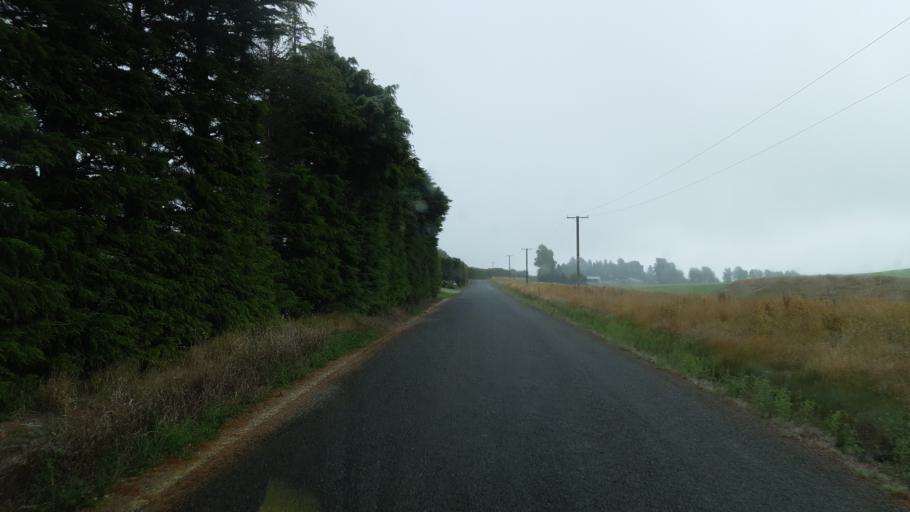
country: NZ
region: Otago
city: Oamaru
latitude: -44.9387
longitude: 170.7270
